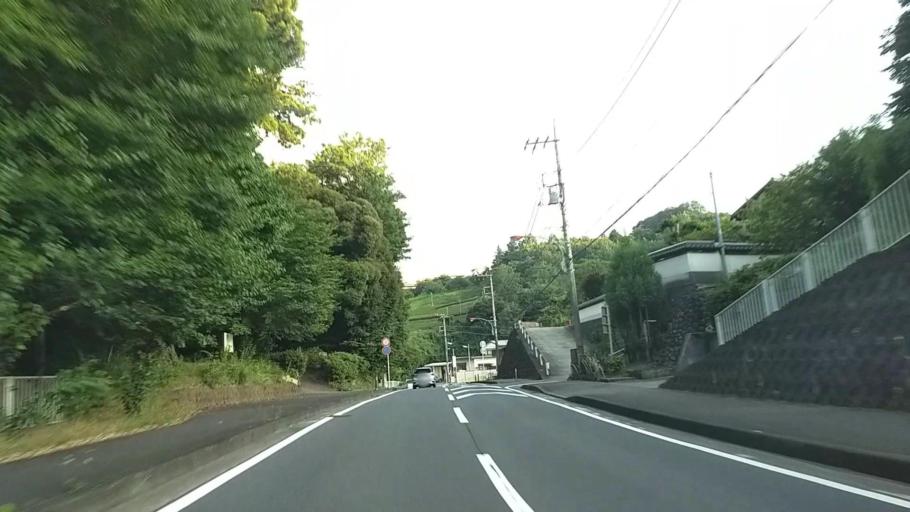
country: JP
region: Kanagawa
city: Atsugi
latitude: 35.4742
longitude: 139.2849
